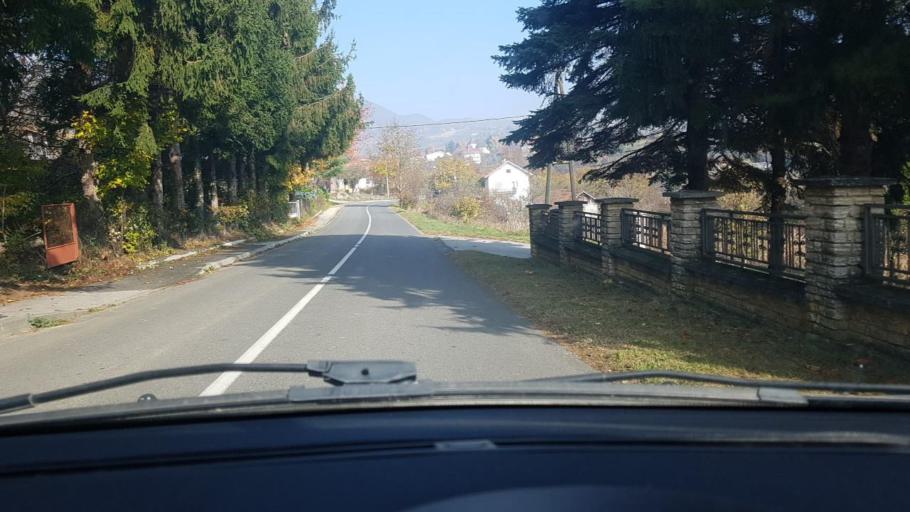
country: HR
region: Krapinsko-Zagorska
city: Zlatar
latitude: 46.1325
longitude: 16.1215
